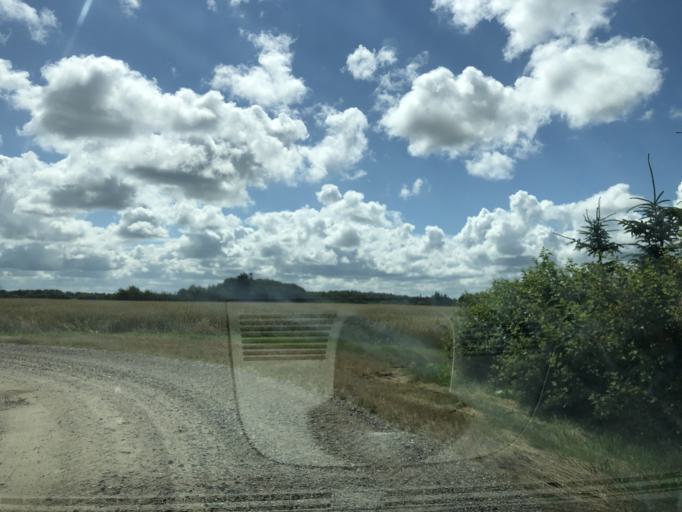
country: DK
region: Central Jutland
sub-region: Holstebro Kommune
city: Ulfborg
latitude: 56.3567
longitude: 8.3700
